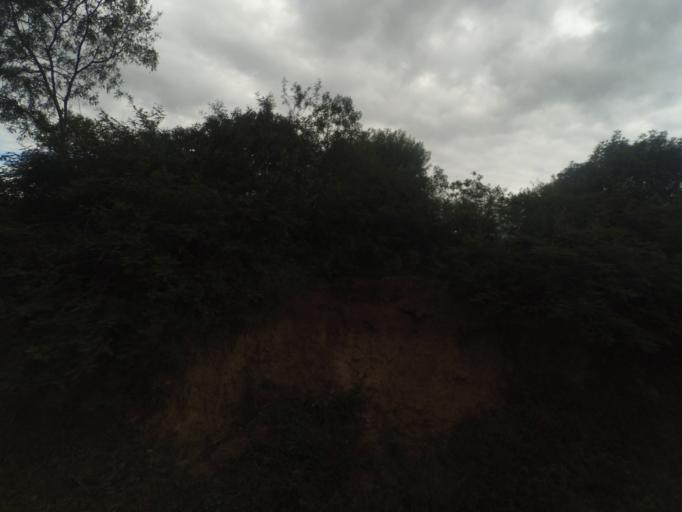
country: BO
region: Santa Cruz
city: Samaipata
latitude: -18.1706
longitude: -63.8426
